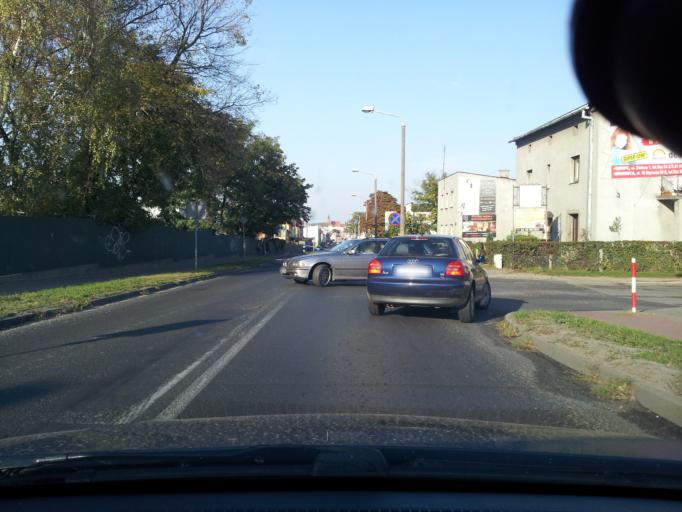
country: PL
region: Kujawsko-Pomorskie
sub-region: Powiat brodnicki
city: Brodnica
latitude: 53.2451
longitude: 19.3970
